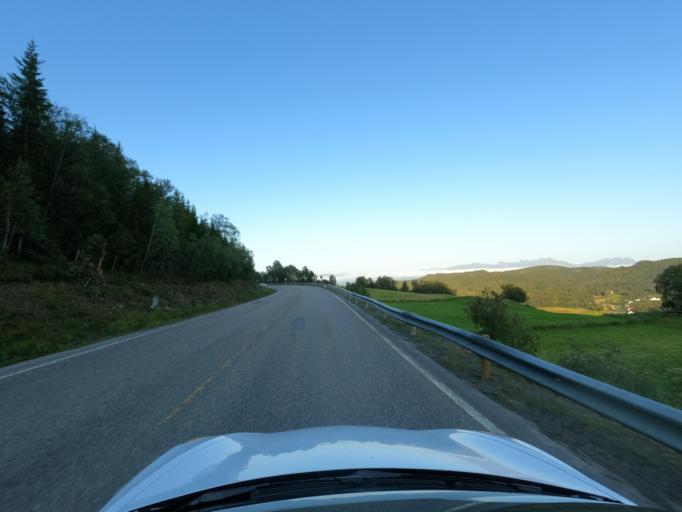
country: NO
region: Troms
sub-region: Harstad
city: Harstad
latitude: 68.7213
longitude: 16.5266
